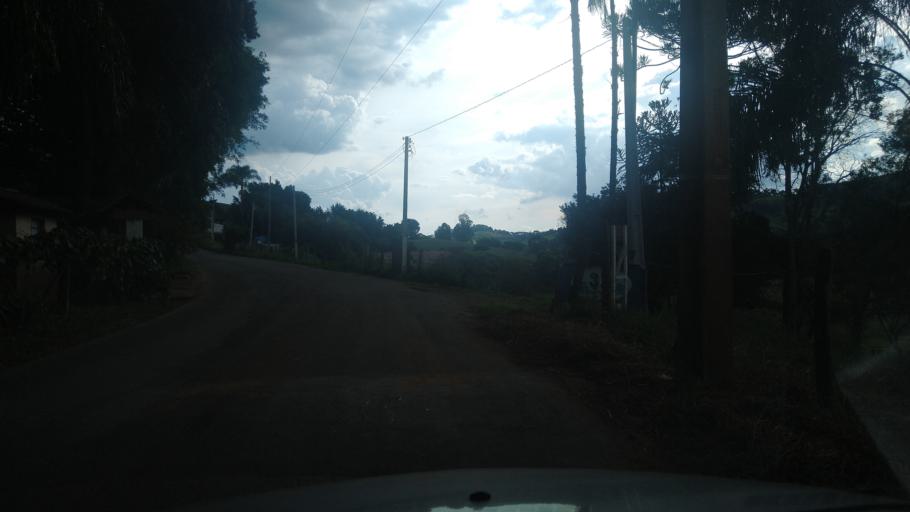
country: BR
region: Minas Gerais
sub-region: Extrema
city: Extrema
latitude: -22.7232
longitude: -46.3483
